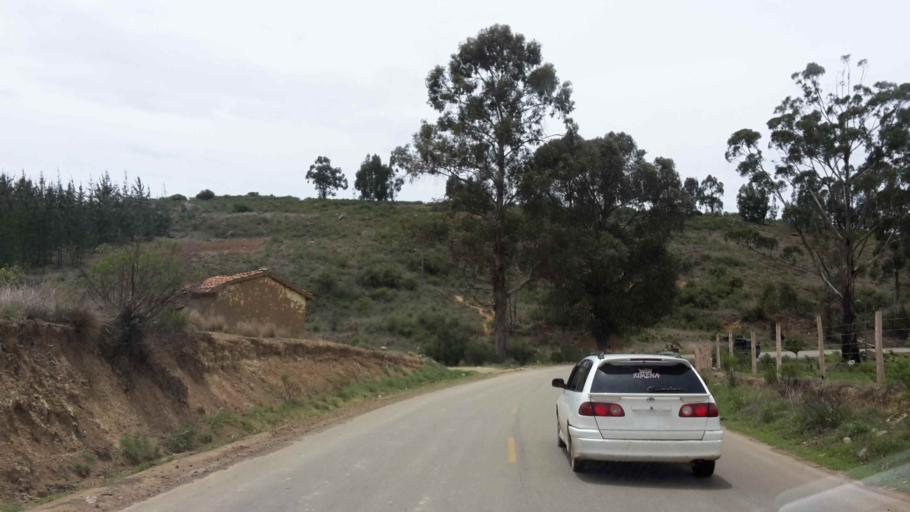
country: BO
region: Cochabamba
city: Totora
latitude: -17.7209
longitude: -65.2028
